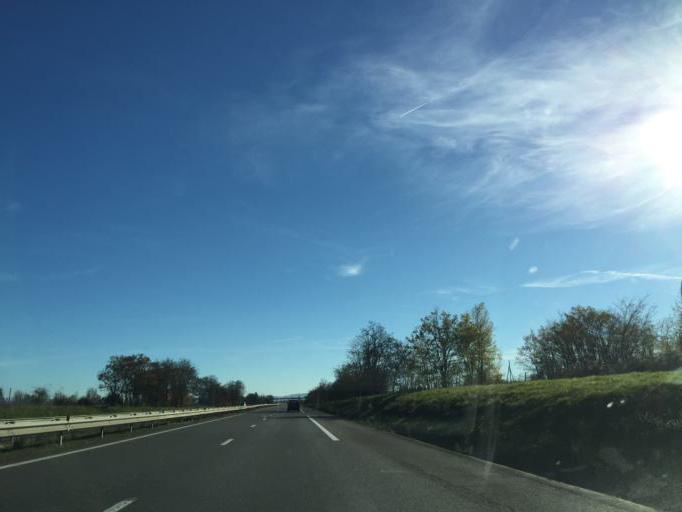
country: FR
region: Rhone-Alpes
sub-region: Departement de la Loire
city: Cuzieu
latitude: 45.5975
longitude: 4.2101
